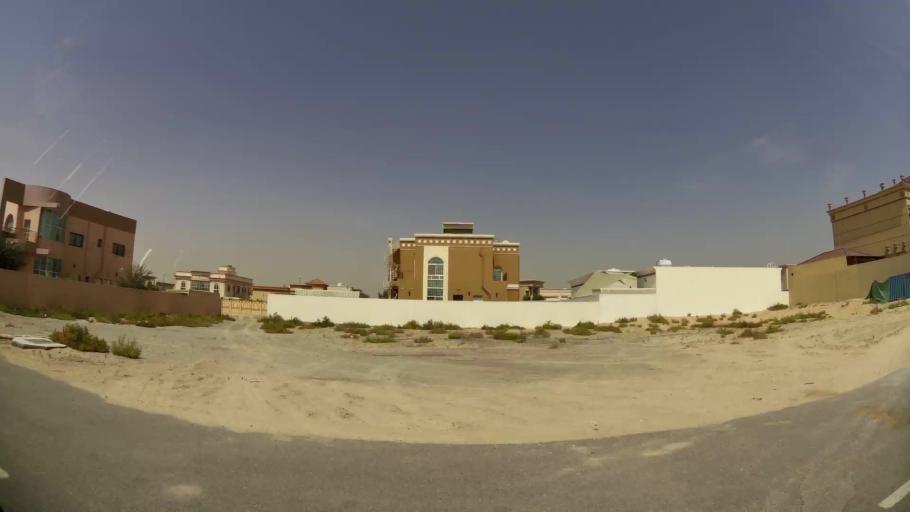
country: AE
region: Ash Shariqah
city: Sharjah
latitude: 25.1866
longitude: 55.4208
